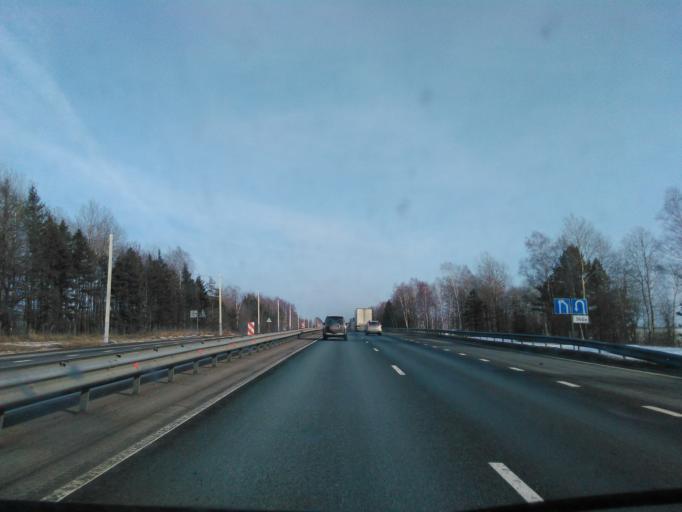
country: RU
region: Smolensk
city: Verkhnedneprovskiy
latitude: 55.1820
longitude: 33.5506
